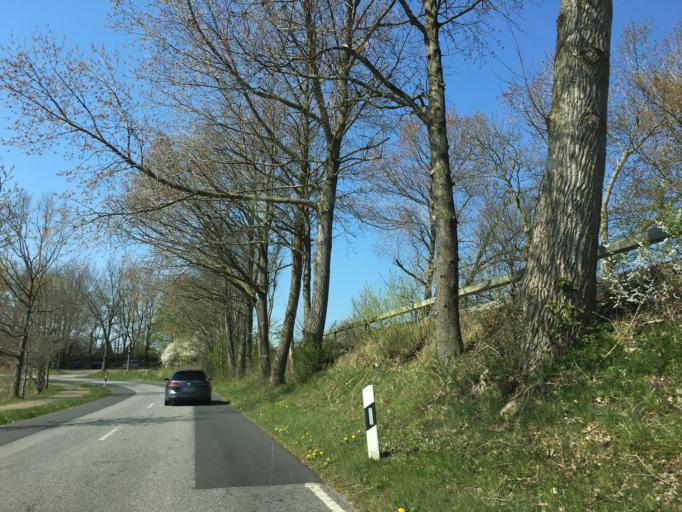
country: DE
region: Schleswig-Holstein
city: Dollrottfeld
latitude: 54.5894
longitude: 9.8114
